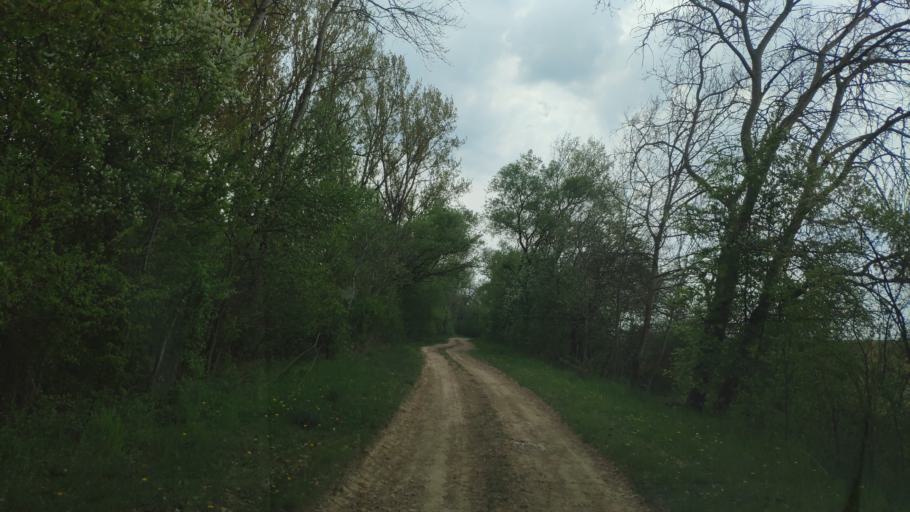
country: SK
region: Kosicky
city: Moldava nad Bodvou
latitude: 48.6108
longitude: 21.0397
